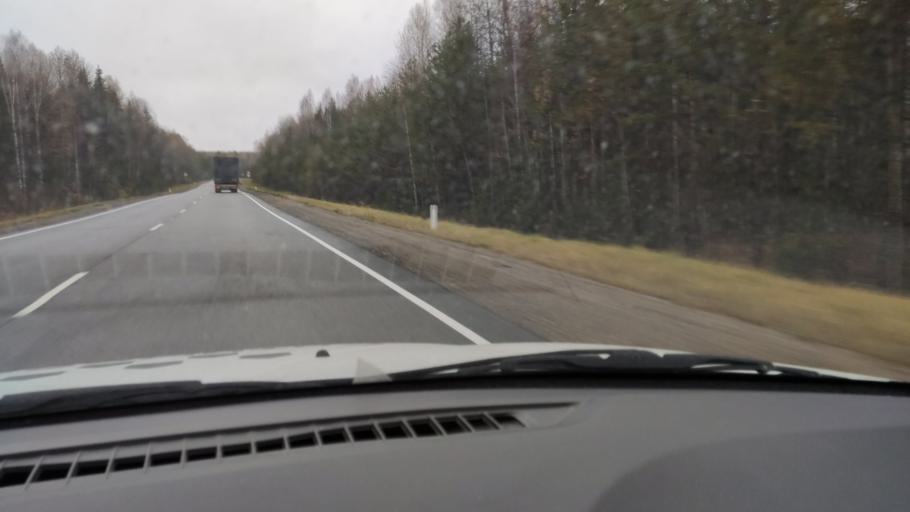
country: RU
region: Kirov
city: Chernaya Kholunitsa
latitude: 58.8286
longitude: 51.7705
